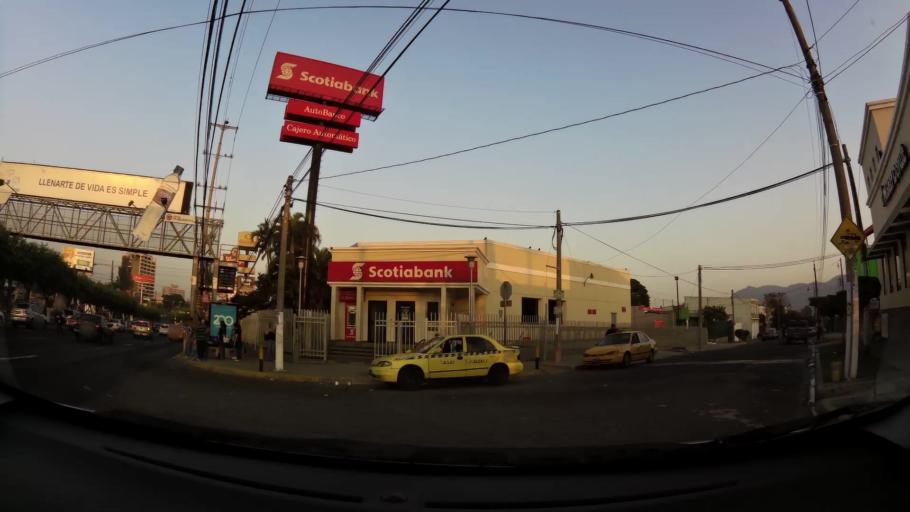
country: SV
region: San Salvador
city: San Salvador
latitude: 13.7089
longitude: -89.2100
